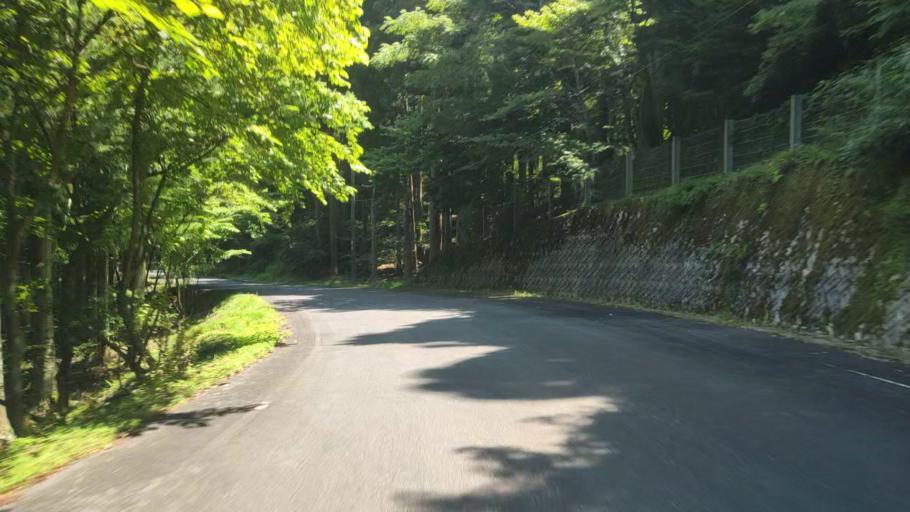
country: JP
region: Fukui
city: Ono
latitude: 35.7225
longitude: 136.5805
